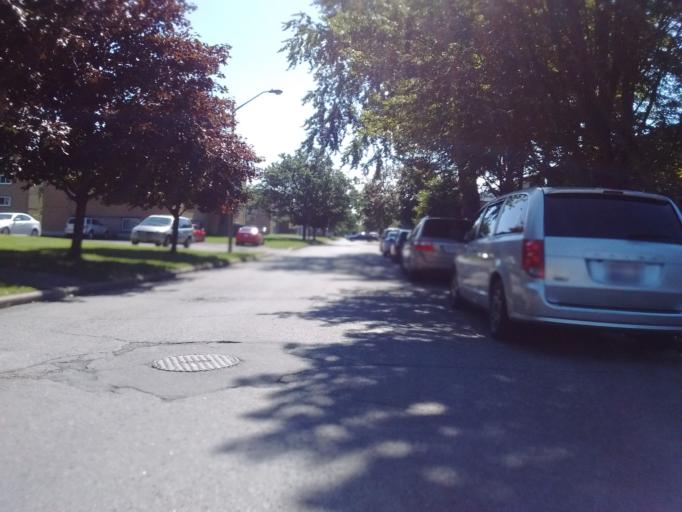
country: CA
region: Ontario
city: Ottawa
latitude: 45.4420
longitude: -75.6413
